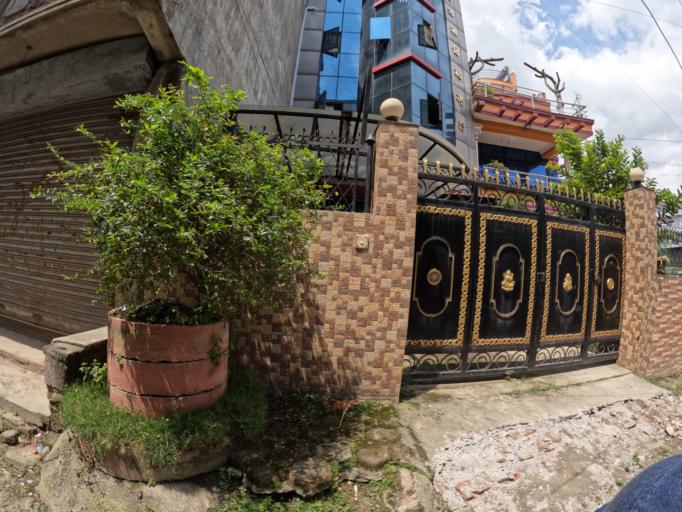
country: NP
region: Central Region
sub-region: Bagmati Zone
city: Bhaktapur
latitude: 27.6753
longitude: 85.3728
